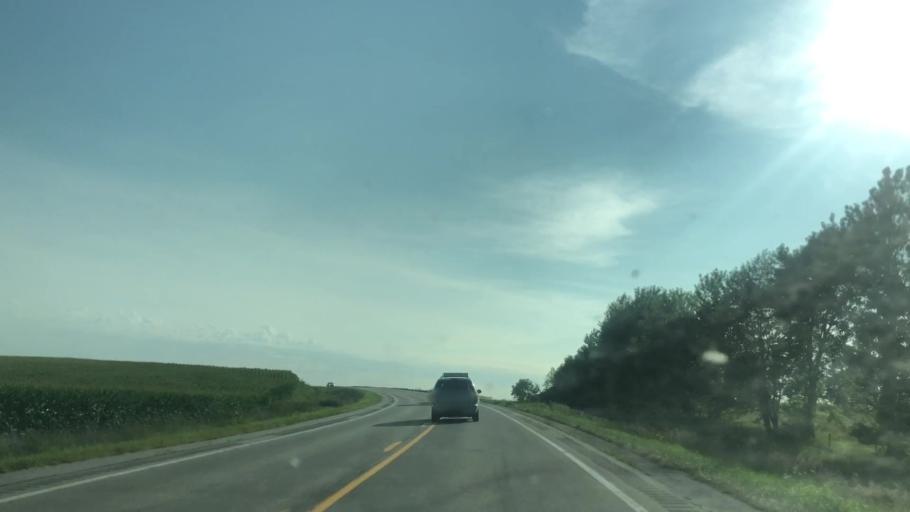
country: US
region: Iowa
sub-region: Marshall County
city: Marshalltown
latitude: 42.0227
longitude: -93.0076
